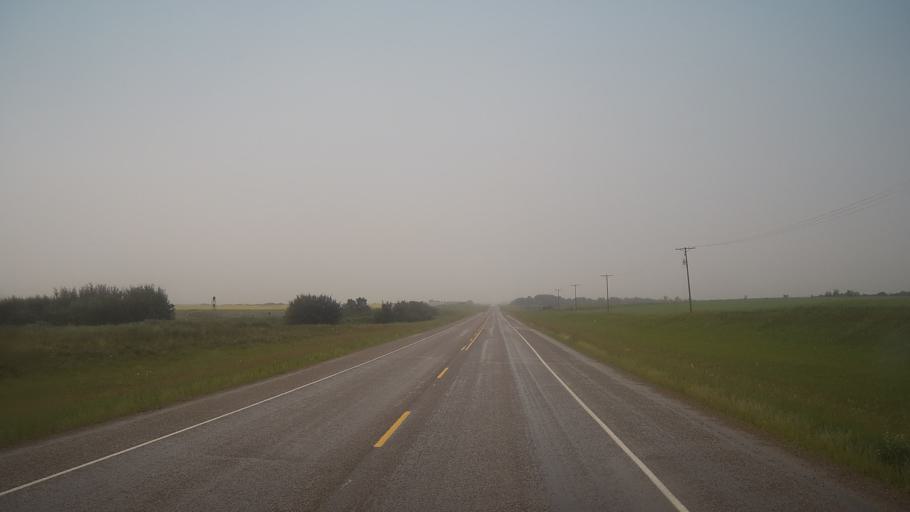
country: CA
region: Saskatchewan
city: Biggar
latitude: 52.1302
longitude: -108.1464
